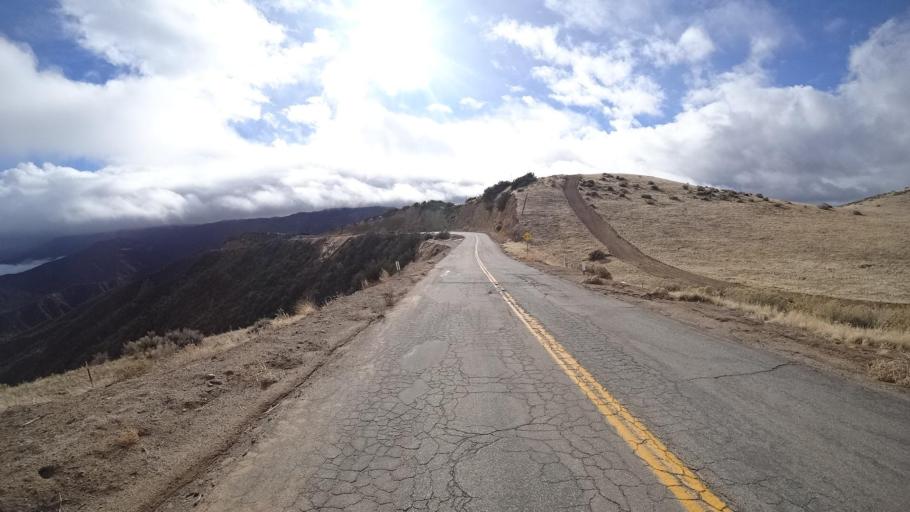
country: US
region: California
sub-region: Kern County
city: Maricopa
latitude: 34.8977
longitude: -119.3659
